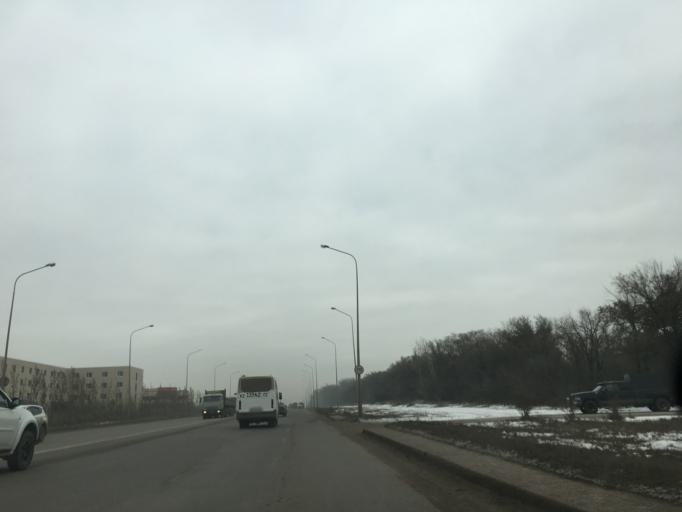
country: KZ
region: Astana Qalasy
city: Astana
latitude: 51.1702
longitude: 71.4923
